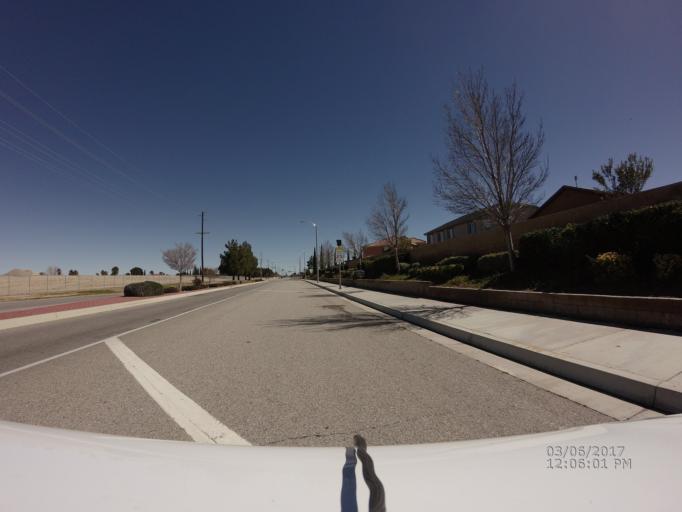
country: US
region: California
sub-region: Los Angeles County
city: Quartz Hill
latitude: 34.6748
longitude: -118.2123
